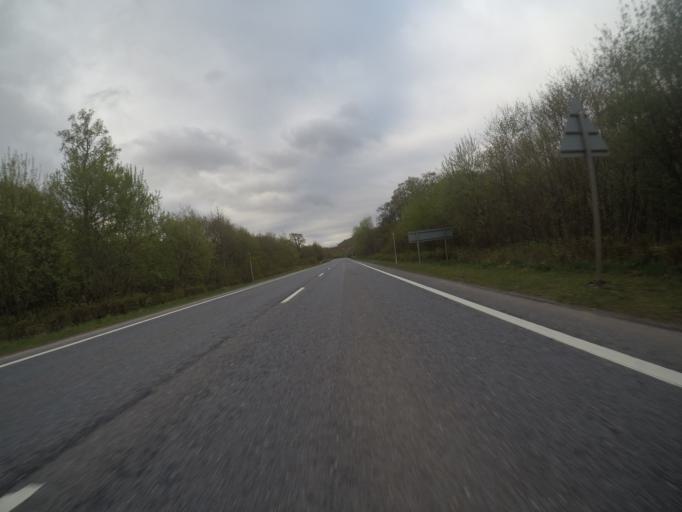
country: GB
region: Scotland
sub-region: Highland
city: Spean Bridge
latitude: 56.9503
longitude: -4.4971
